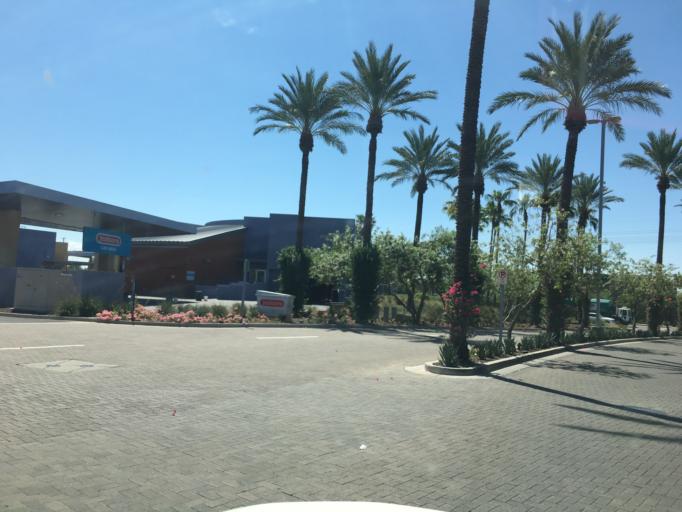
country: US
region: Arizona
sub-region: Maricopa County
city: Tempe
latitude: 33.4303
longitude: -111.9005
